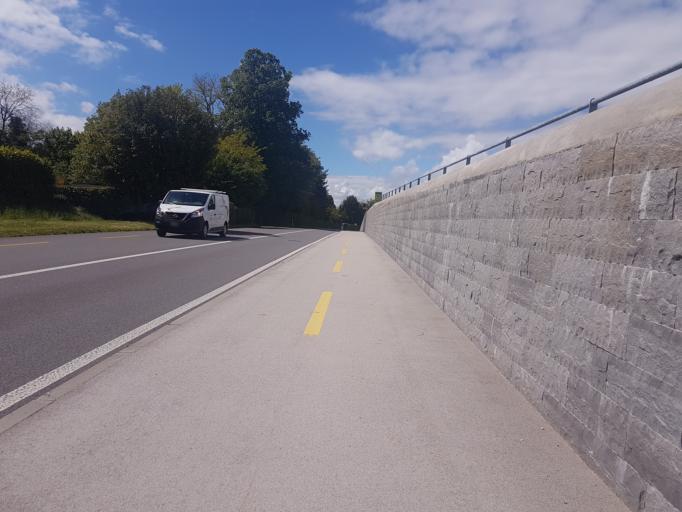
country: CH
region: Vaud
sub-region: Nyon District
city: Gland
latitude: 46.4292
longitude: 6.2999
